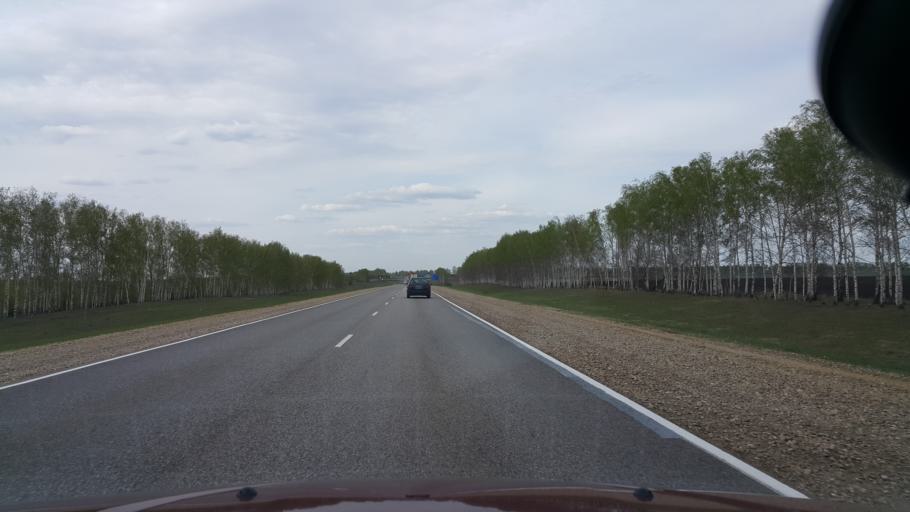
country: RU
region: Tambov
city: Pokrovo-Prigorodnoye
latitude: 52.6507
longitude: 41.3407
